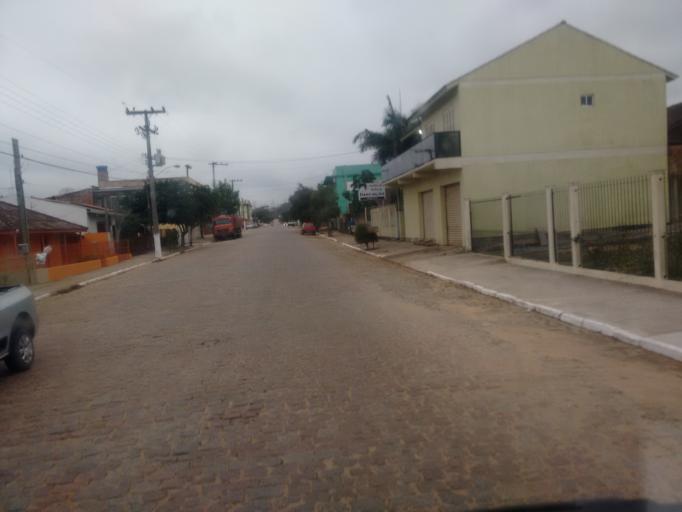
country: BR
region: Rio Grande do Sul
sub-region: Camaqua
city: Camaqua
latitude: -30.8411
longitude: -51.8151
